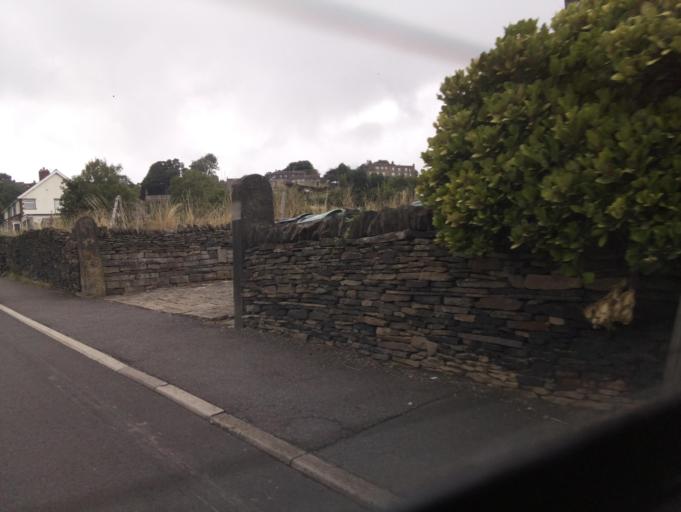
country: GB
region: England
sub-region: Kirklees
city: Shelley
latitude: 53.5942
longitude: -1.6898
